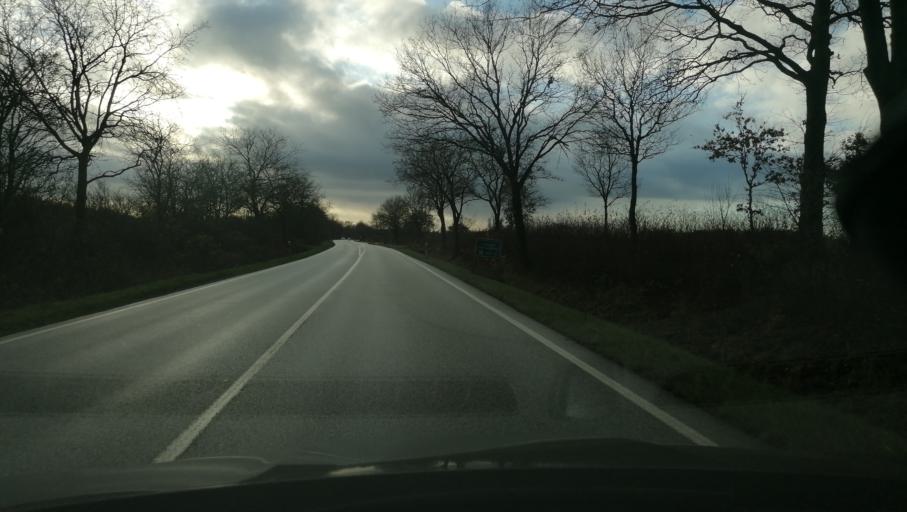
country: DE
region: Schleswig-Holstein
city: Sarzbuttel
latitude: 54.1083
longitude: 9.1982
